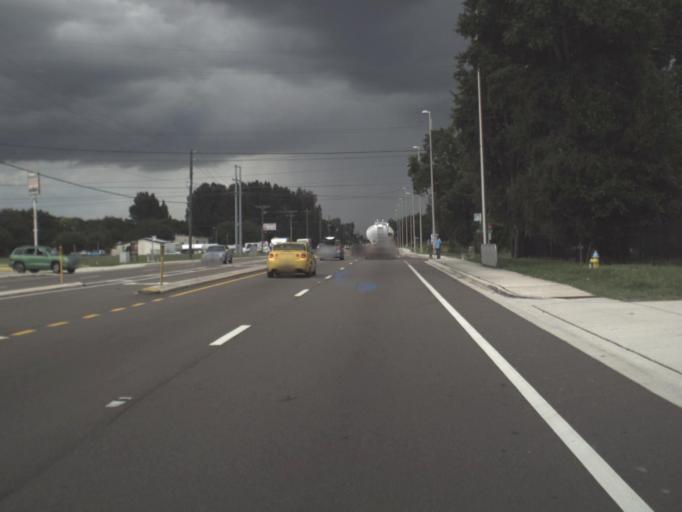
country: US
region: Florida
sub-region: Hillsborough County
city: Palm River-Clair Mel
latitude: 27.9226
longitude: -82.3631
